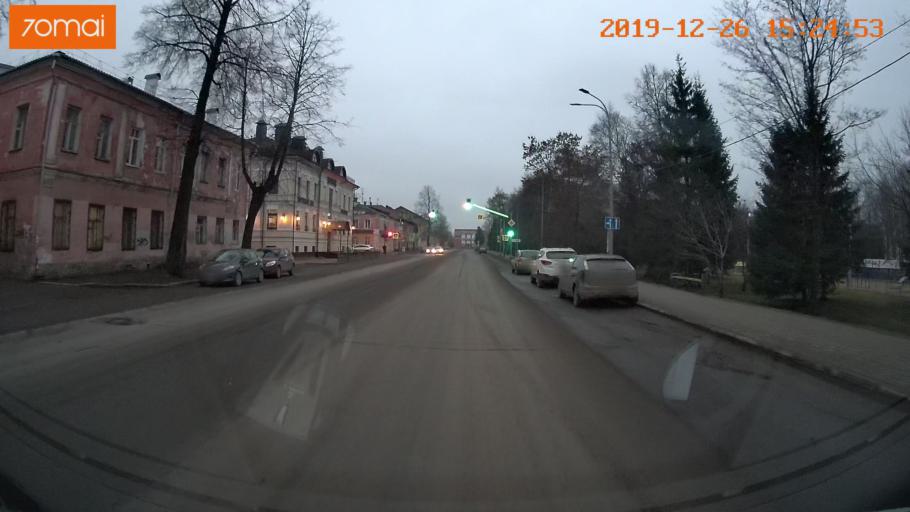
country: RU
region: Jaroslavl
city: Rybinsk
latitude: 58.0518
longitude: 38.8437
